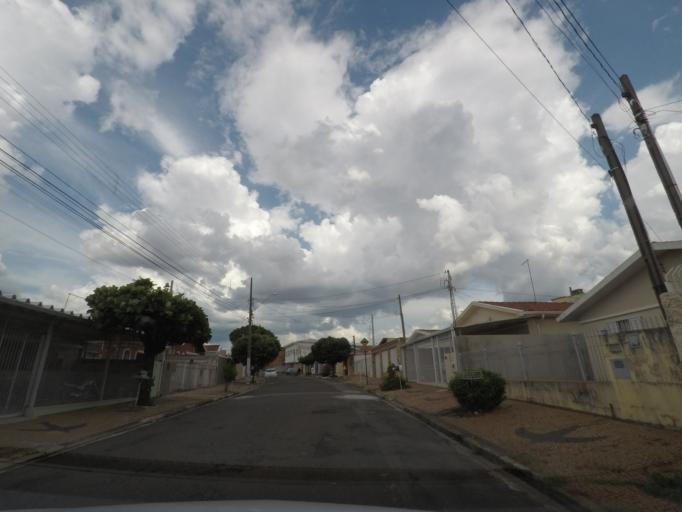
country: BR
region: Sao Paulo
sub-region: Campinas
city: Campinas
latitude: -22.8975
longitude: -47.1051
